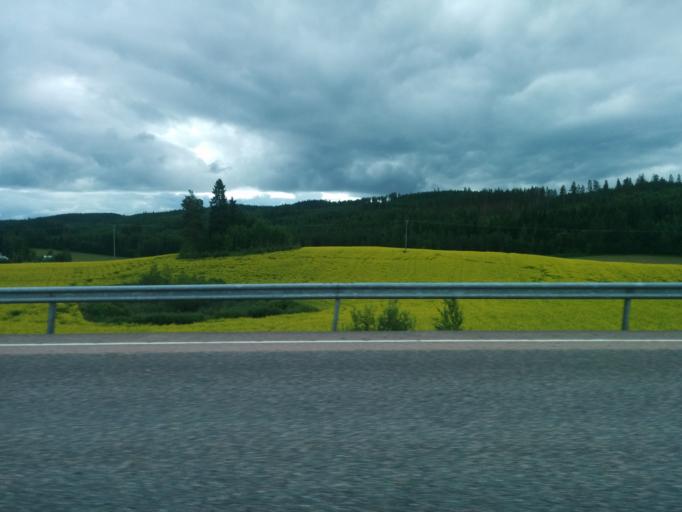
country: FI
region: Pirkanmaa
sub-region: Tampere
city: Orivesi
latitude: 61.7007
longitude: 24.4333
